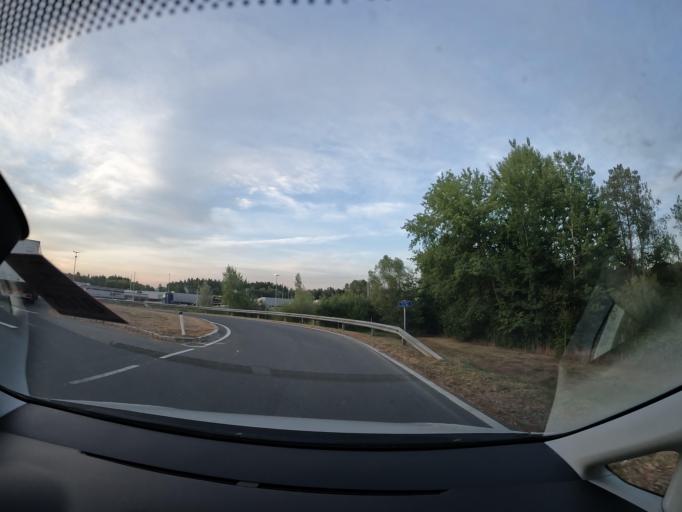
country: AT
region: Styria
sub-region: Politischer Bezirk Graz-Umgebung
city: Unterpremstatten
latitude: 46.9584
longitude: 15.3833
